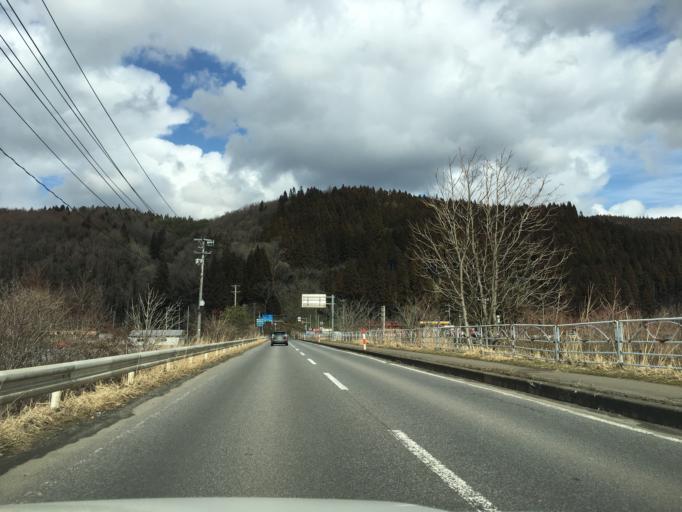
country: JP
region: Akita
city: Odate
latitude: 40.2286
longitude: 140.5915
